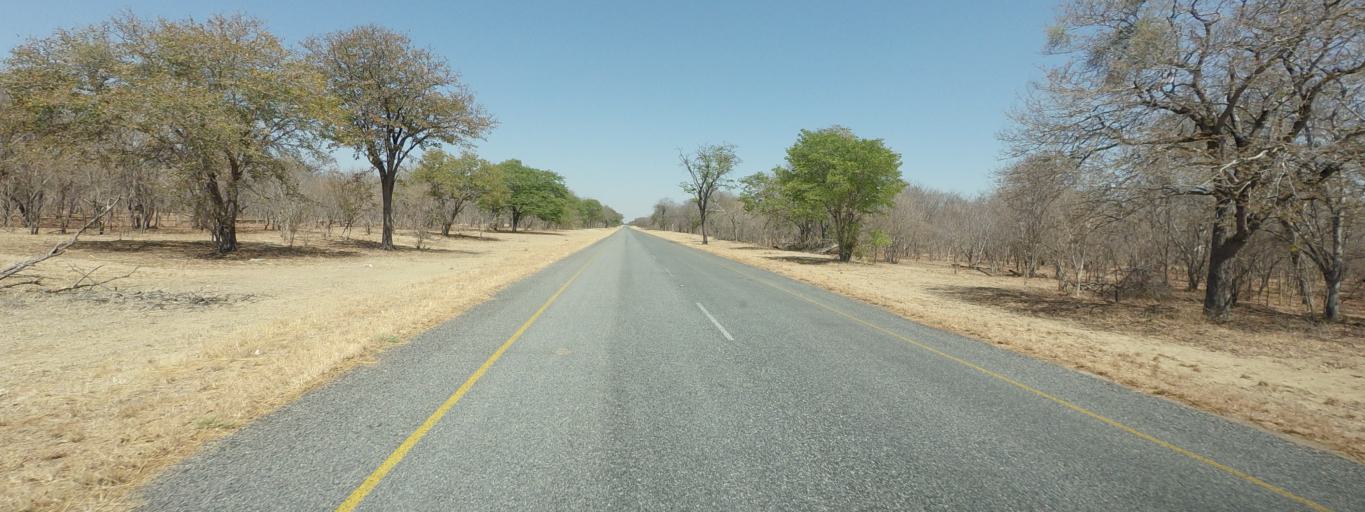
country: BW
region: North West
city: Kasane
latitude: -17.9277
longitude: 24.7512
